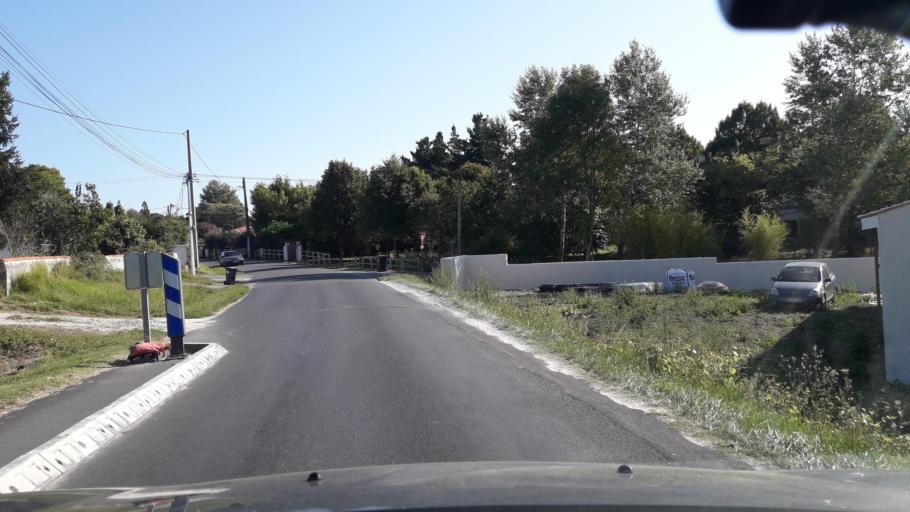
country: FR
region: Poitou-Charentes
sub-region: Departement de la Charente-Maritime
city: Etaules
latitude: 45.7129
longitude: -1.1107
